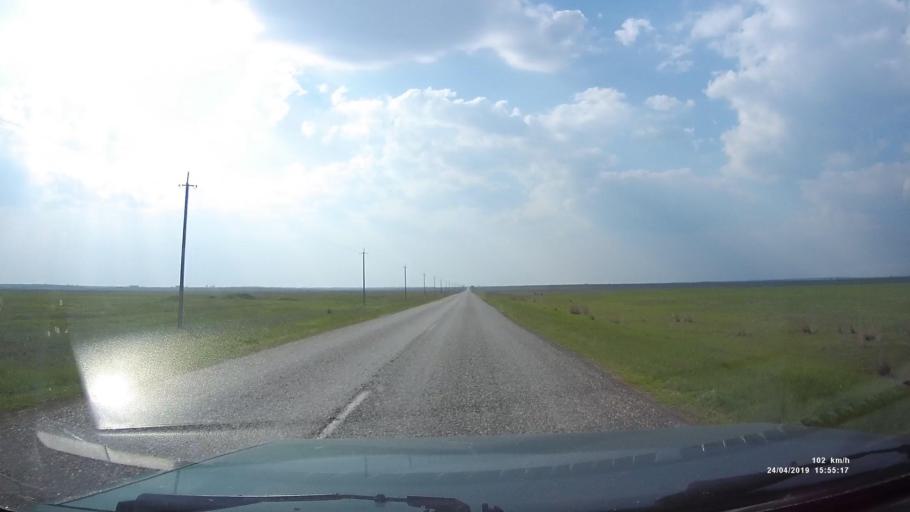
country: RU
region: Kalmykiya
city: Yashalta
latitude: 46.5894
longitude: 42.5523
